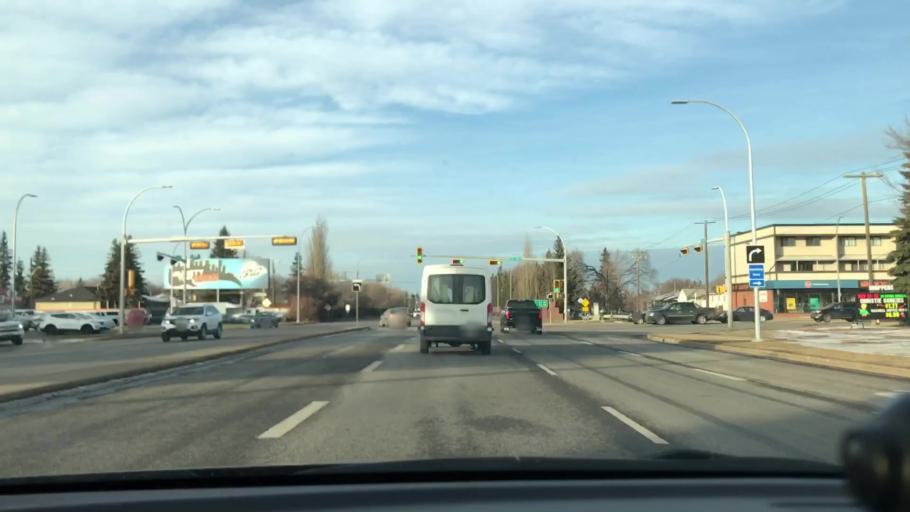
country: CA
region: Alberta
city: Edmonton
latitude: 53.5406
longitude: -113.4434
